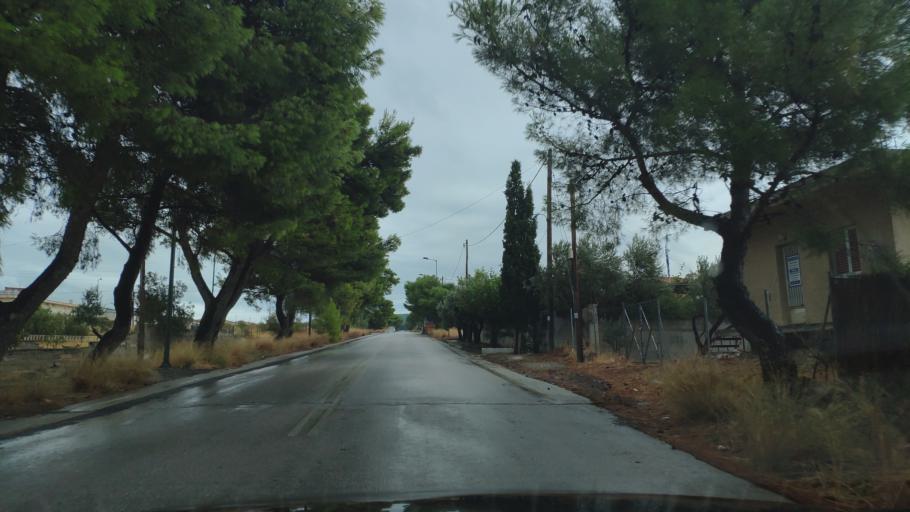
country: GR
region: Peloponnese
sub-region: Nomos Korinthias
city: Loutraki
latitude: 37.9665
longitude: 22.9854
